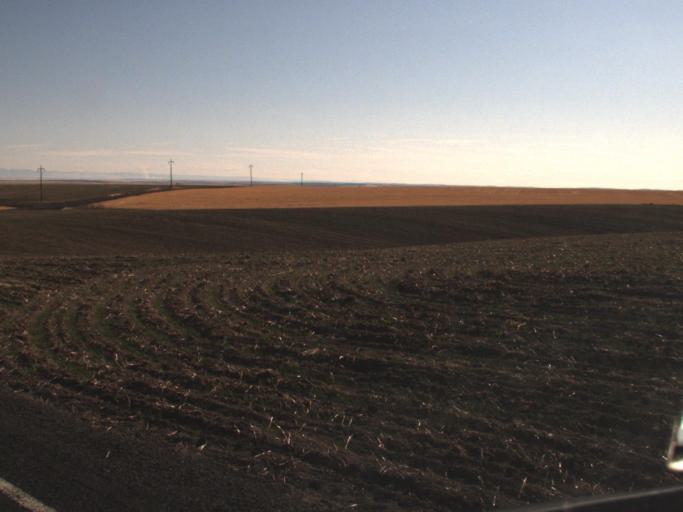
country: US
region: Washington
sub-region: Adams County
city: Ritzville
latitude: 46.8715
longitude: -118.5490
